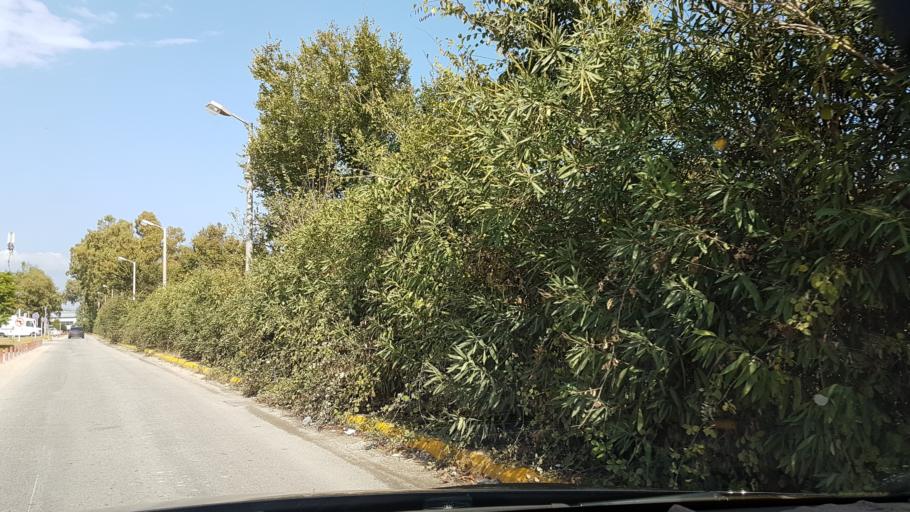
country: GR
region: Ionian Islands
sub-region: Nomos Kerkyras
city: Kerkyra
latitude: 39.6064
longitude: 19.9155
